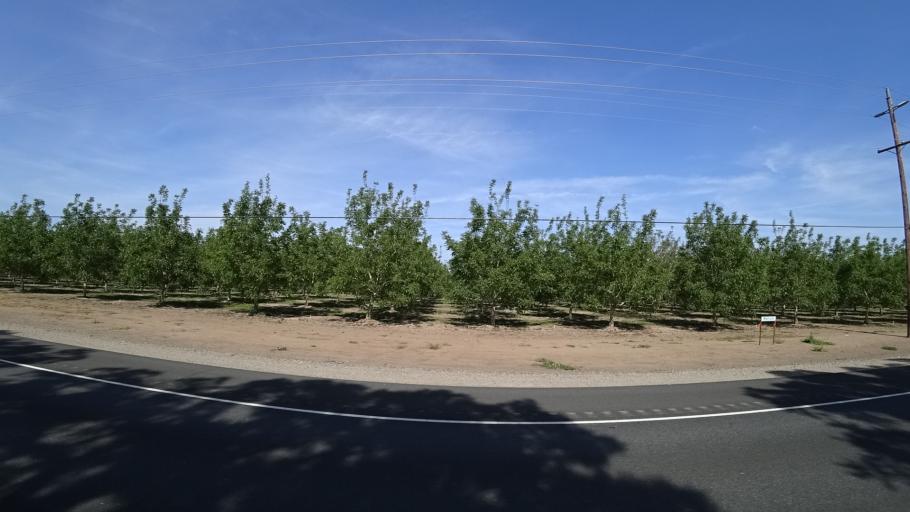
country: US
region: California
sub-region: Glenn County
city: Hamilton City
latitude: 39.8719
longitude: -121.9675
